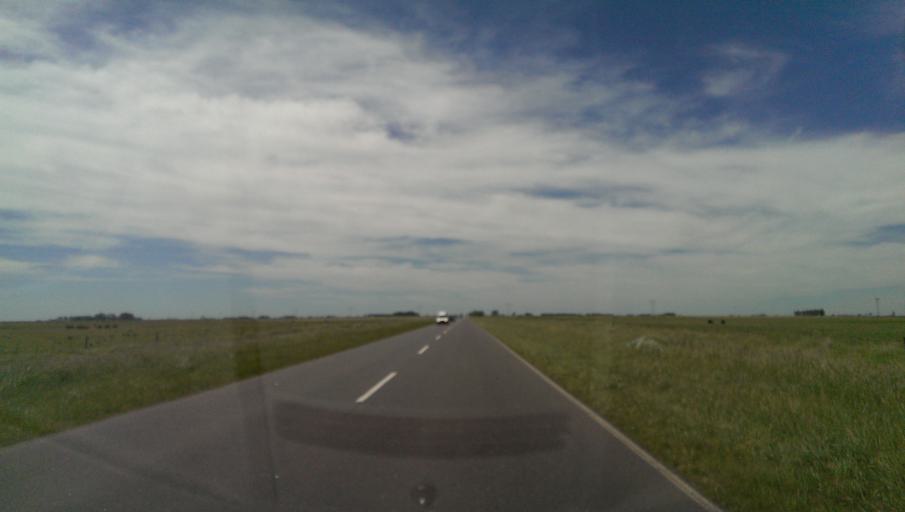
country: AR
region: Buenos Aires
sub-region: Partido de Laprida
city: Laprida
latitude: -37.2379
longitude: -60.7432
